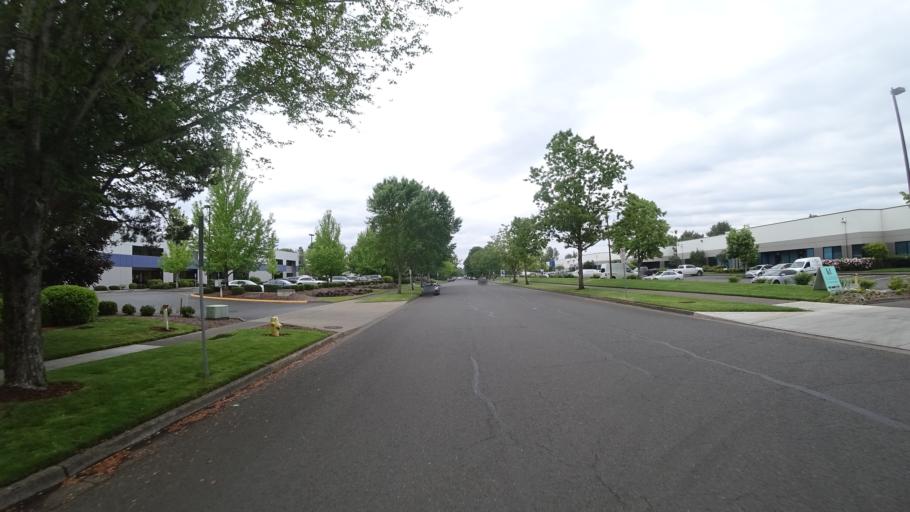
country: US
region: Oregon
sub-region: Washington County
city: Raleigh Hills
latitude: 45.4798
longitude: -122.7787
